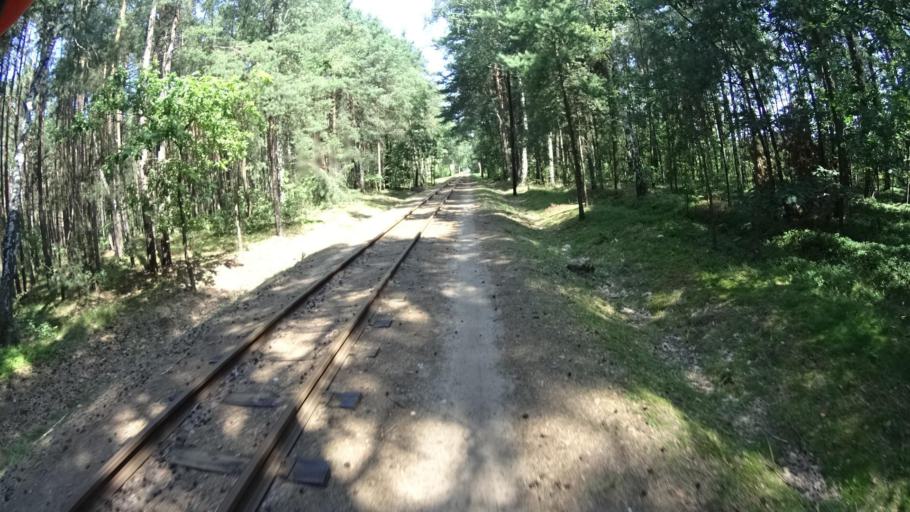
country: PL
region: Masovian Voivodeship
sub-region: Powiat piaseczynski
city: Lesznowola
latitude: 52.0153
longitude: 20.9282
